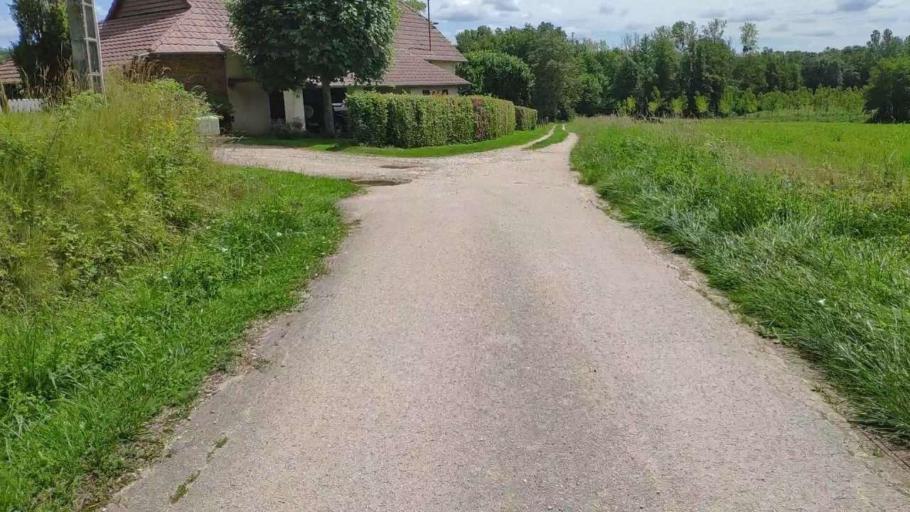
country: FR
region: Franche-Comte
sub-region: Departement du Jura
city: Chaussin
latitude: 46.9007
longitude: 5.4513
